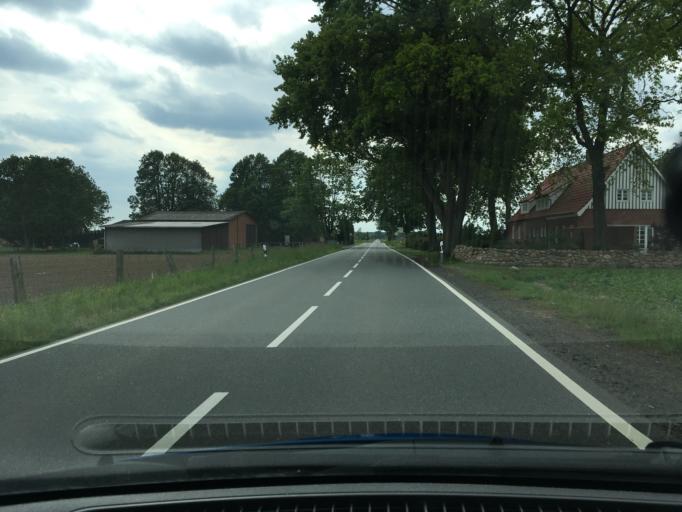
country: DE
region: Lower Saxony
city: Betzendorf
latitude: 53.1031
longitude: 10.2786
